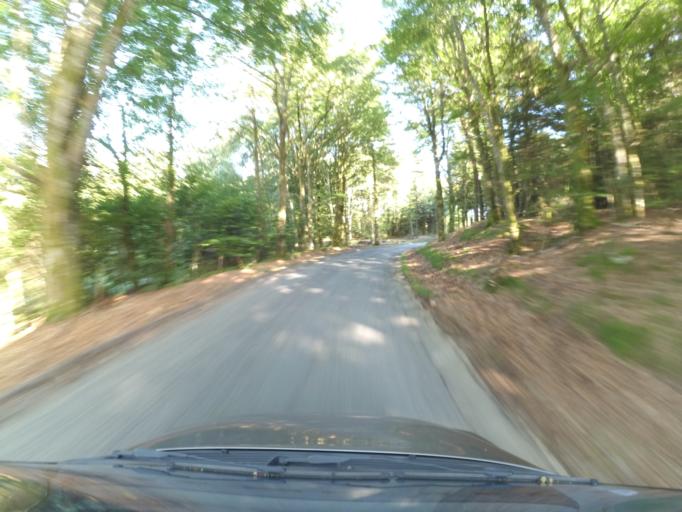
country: FR
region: Limousin
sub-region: Departement de la Creuse
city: Banize
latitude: 45.7843
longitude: 1.9732
